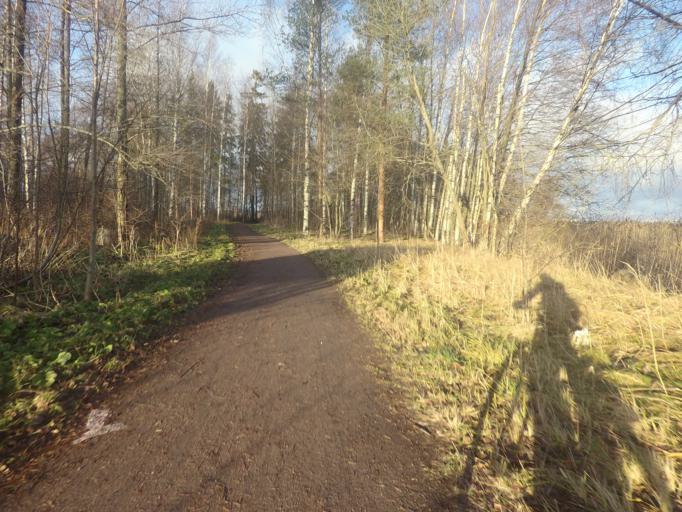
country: FI
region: Uusimaa
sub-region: Helsinki
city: Teekkarikylae
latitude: 60.1919
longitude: 24.8383
